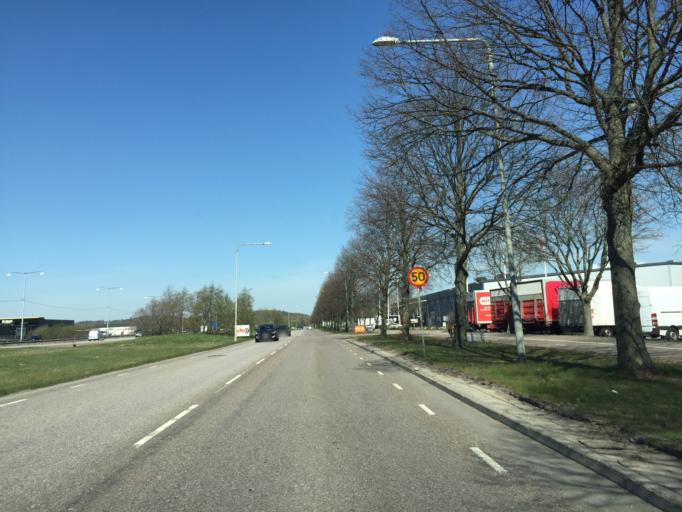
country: SE
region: Vaestra Goetaland
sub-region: Goteborg
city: Hammarkullen
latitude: 57.7783
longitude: 11.9993
